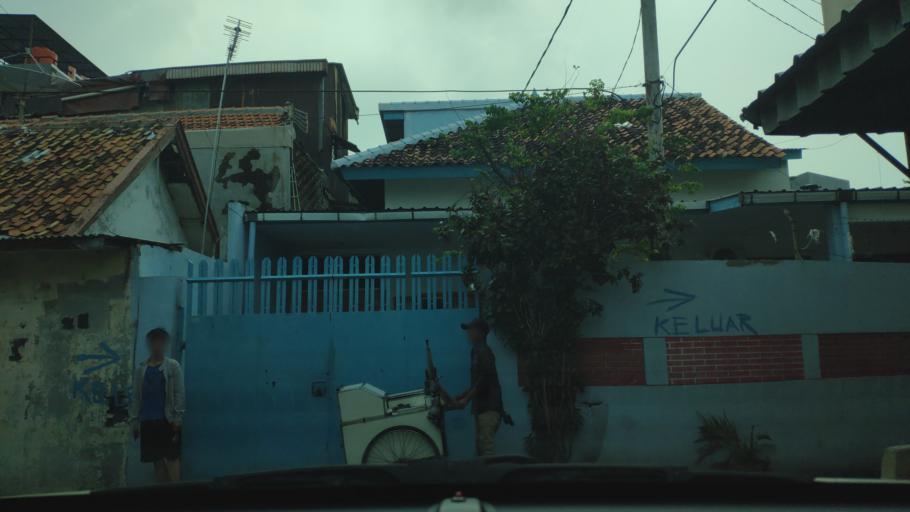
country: ID
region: Jakarta Raya
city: Jakarta
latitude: -6.1585
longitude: 106.8125
